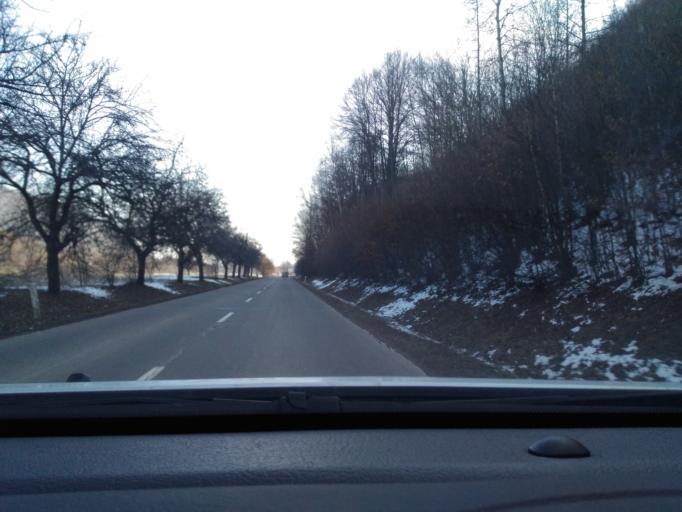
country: CZ
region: South Moravian
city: Predklasteri
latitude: 49.3665
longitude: 16.3931
